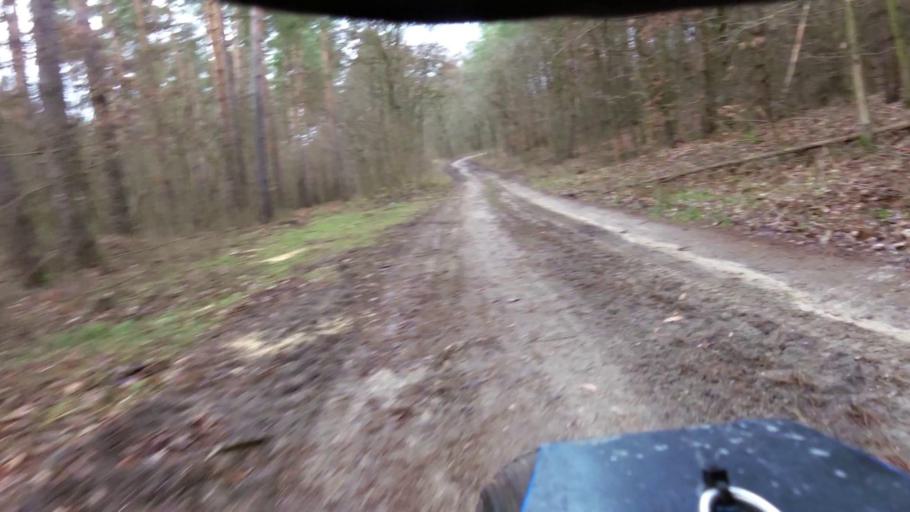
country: PL
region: Lubusz
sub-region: Powiat gorzowski
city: Jenin
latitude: 52.7169
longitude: 15.1266
